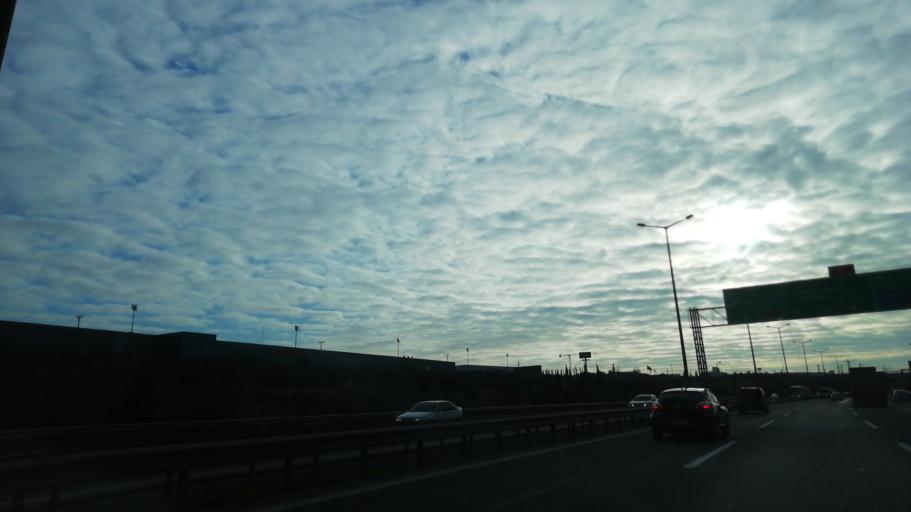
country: TR
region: Kocaeli
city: Balcik
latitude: 40.8732
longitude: 29.3928
